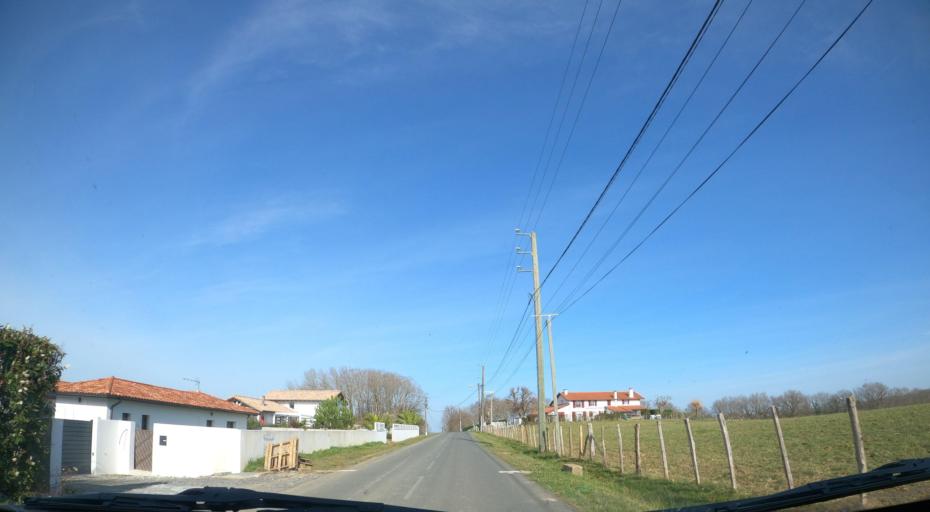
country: FR
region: Aquitaine
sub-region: Departement des Pyrenees-Atlantiques
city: Lahonce
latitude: 43.4383
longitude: -1.3759
